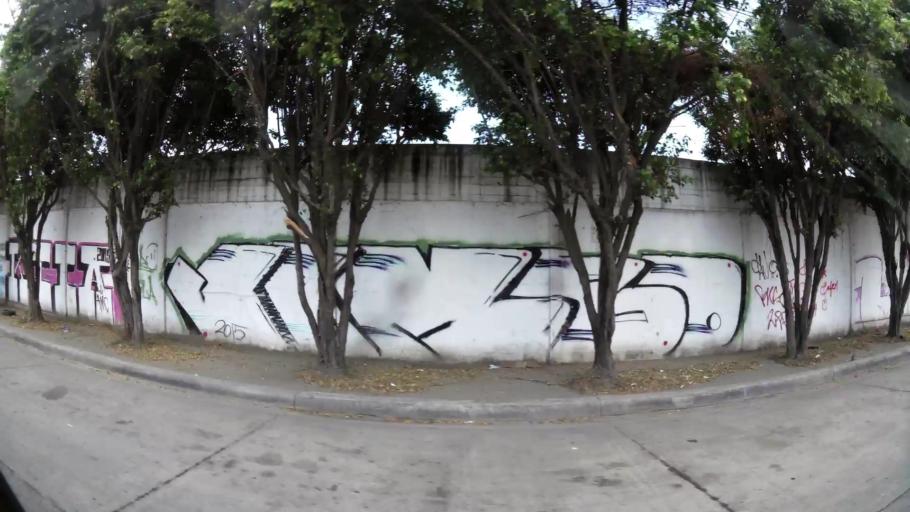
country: EC
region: Guayas
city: Guayaquil
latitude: -2.1222
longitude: -79.9295
